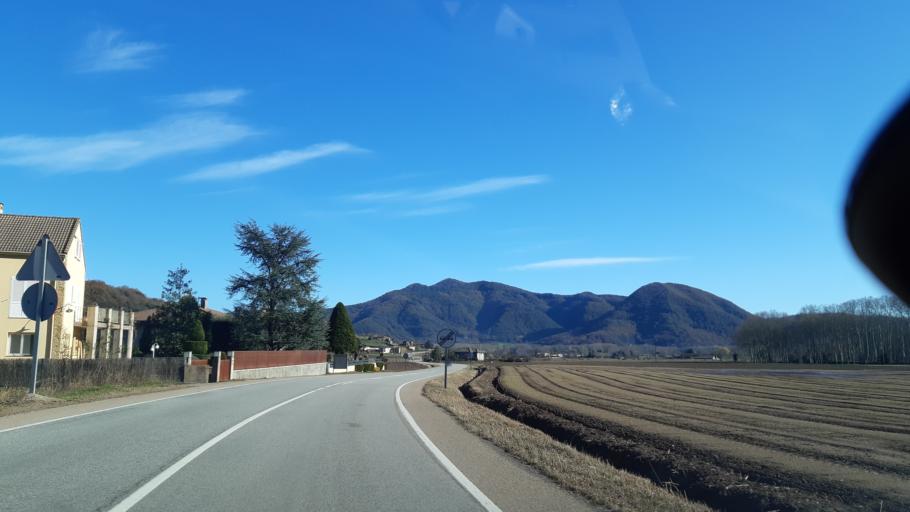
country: ES
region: Catalonia
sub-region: Provincia de Girona
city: Bas
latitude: 42.1500
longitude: 2.4260
